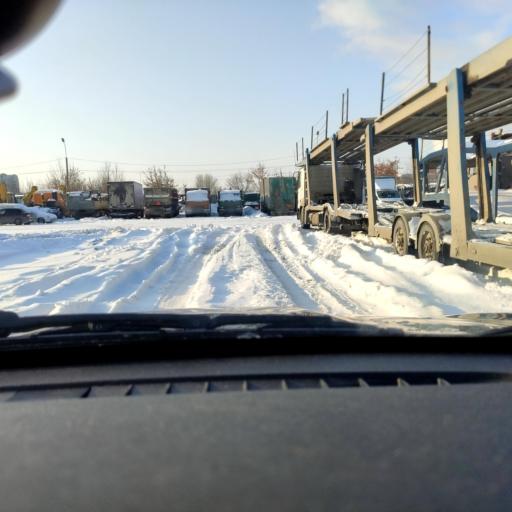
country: RU
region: Samara
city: Tol'yatti
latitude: 53.5513
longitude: 49.3295
